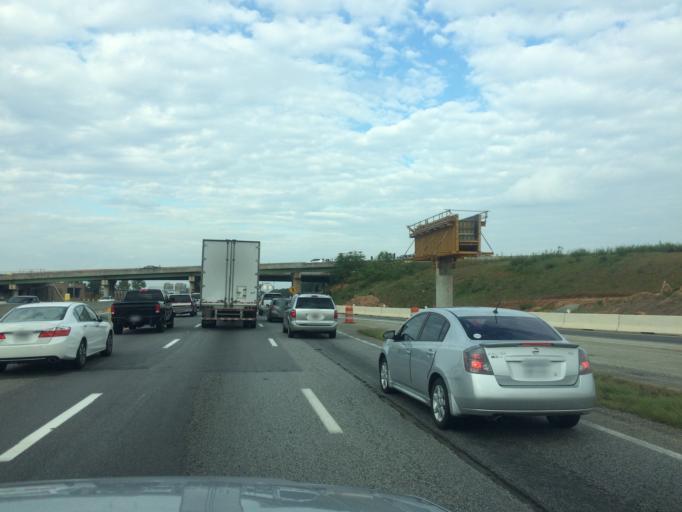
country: US
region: South Carolina
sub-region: Greenville County
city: Mauldin
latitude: 34.8333
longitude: -82.2964
